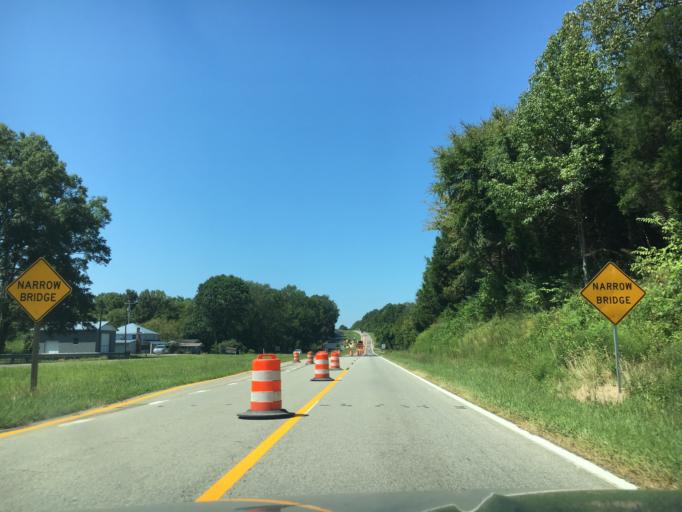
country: US
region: Virginia
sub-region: City of Danville
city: Danville
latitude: 36.5814
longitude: -79.1997
